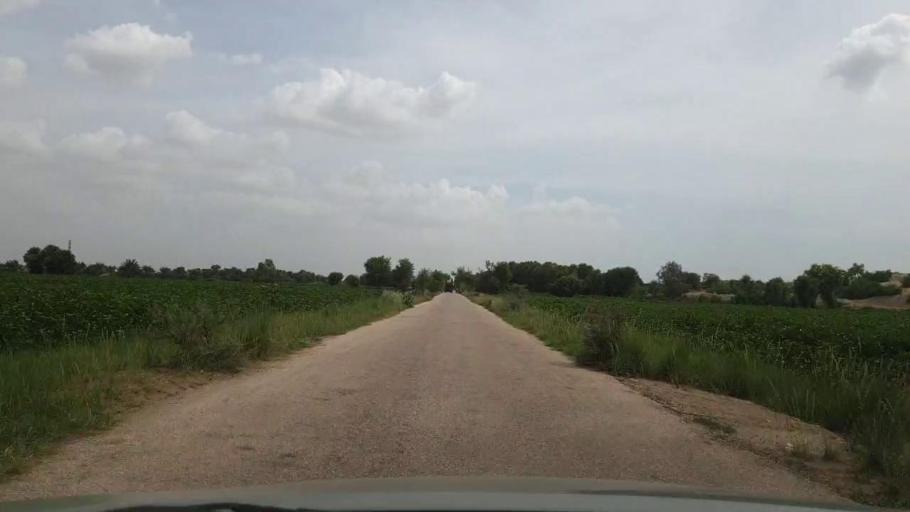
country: PK
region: Sindh
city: Kot Diji
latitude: 27.1591
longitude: 69.0351
